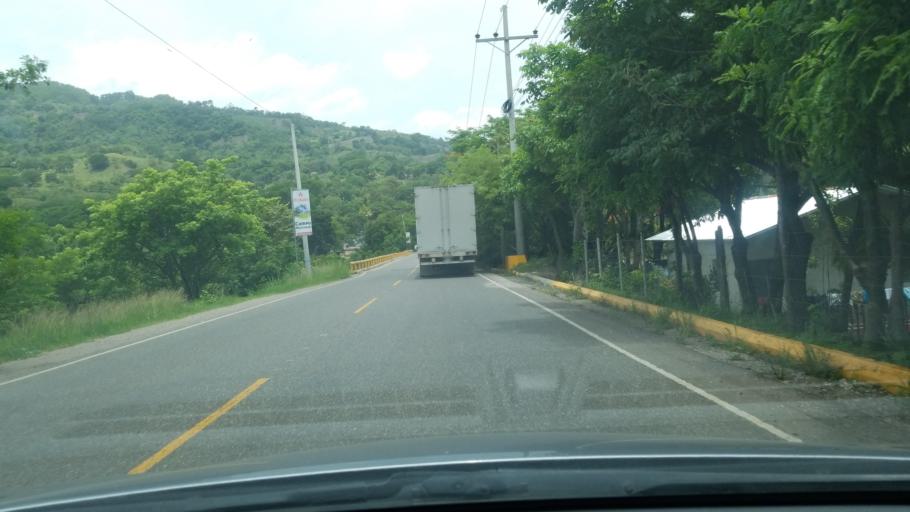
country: HN
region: Copan
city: Ojos de Agua
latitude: 14.7164
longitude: -88.7777
